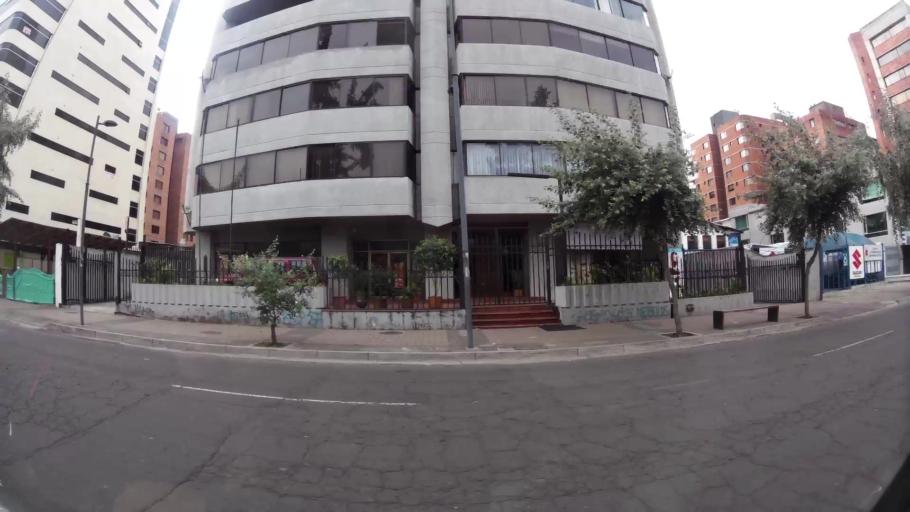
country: EC
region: Pichincha
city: Quito
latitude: -0.1786
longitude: -78.4811
